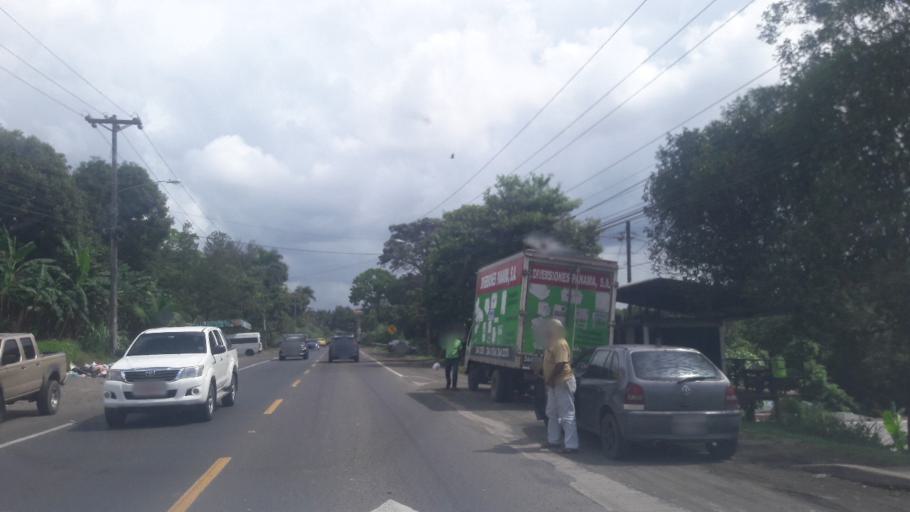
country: PA
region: Panama
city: Alcalde Diaz
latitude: 9.1269
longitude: -79.5809
